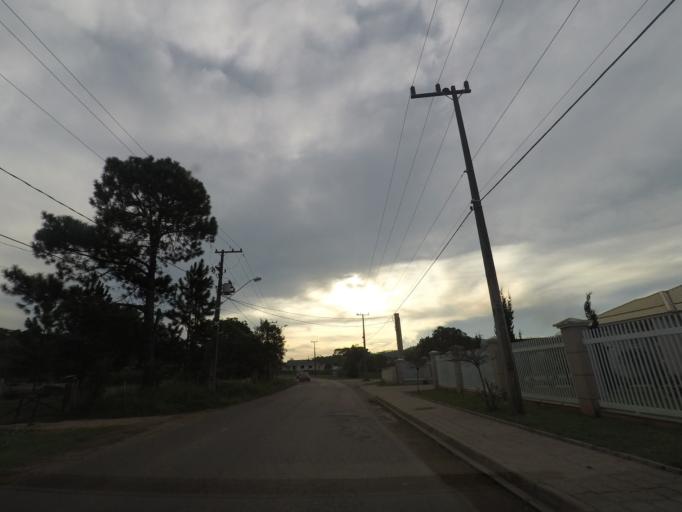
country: BR
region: Parana
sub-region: Colombo
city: Colombo
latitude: -25.2876
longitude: -49.1974
